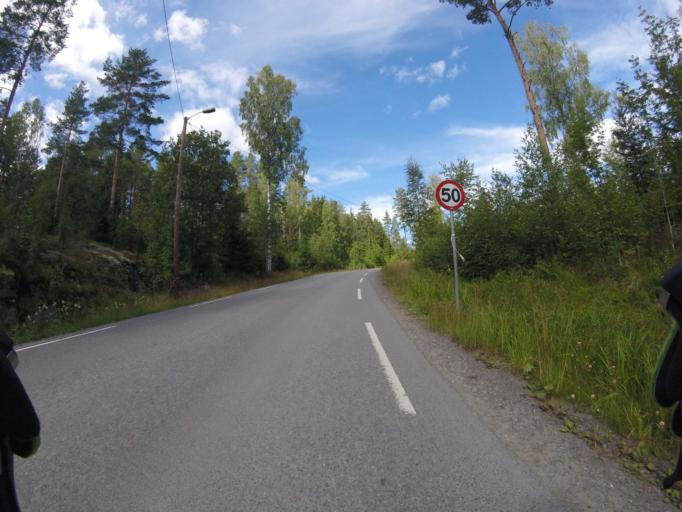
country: NO
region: Akershus
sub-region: Lorenskog
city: Kjenn
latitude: 59.8929
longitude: 10.9756
